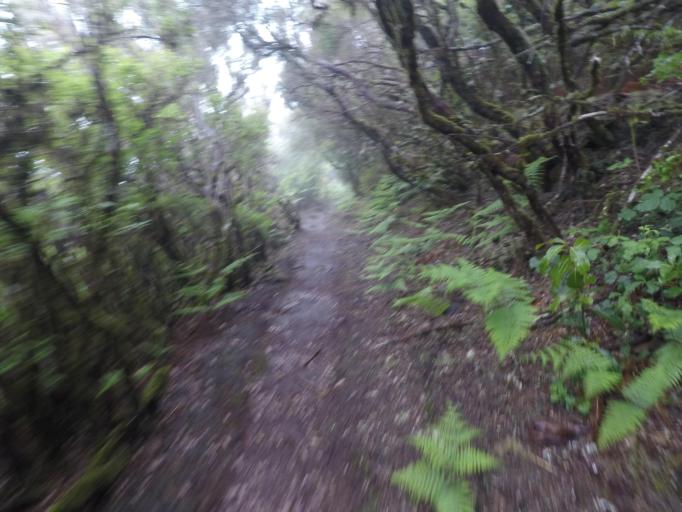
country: PT
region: Madeira
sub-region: Calheta
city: Arco da Calheta
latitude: 32.7690
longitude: -17.1170
